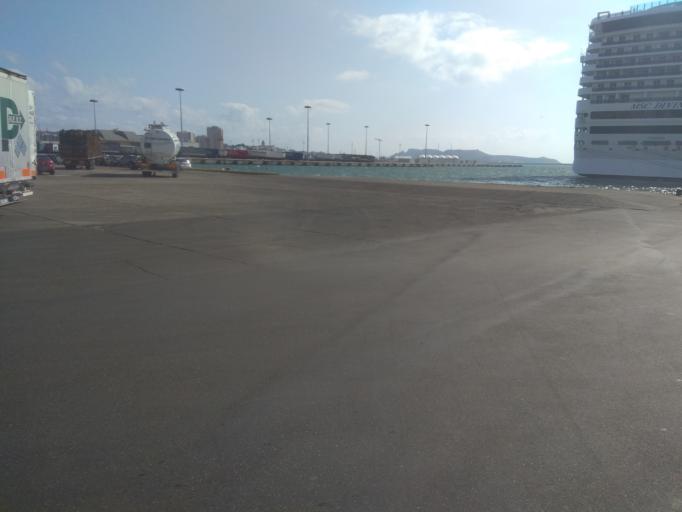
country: IT
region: Sardinia
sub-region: Provincia di Cagliari
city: Cagliari
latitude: 39.2116
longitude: 9.1037
